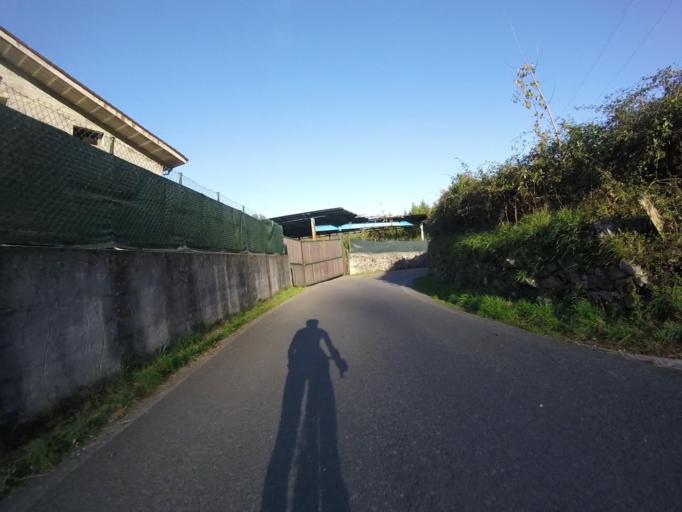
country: ES
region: Navarre
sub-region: Provincia de Navarra
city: Igantzi
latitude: 43.2352
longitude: -1.7018
